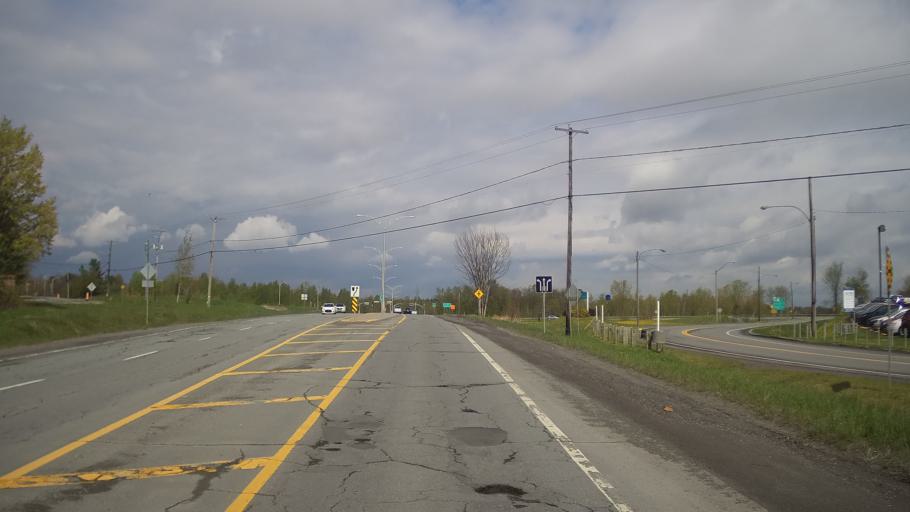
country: CA
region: Quebec
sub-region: Monteregie
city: Cowansville
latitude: 45.2105
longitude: -72.7705
